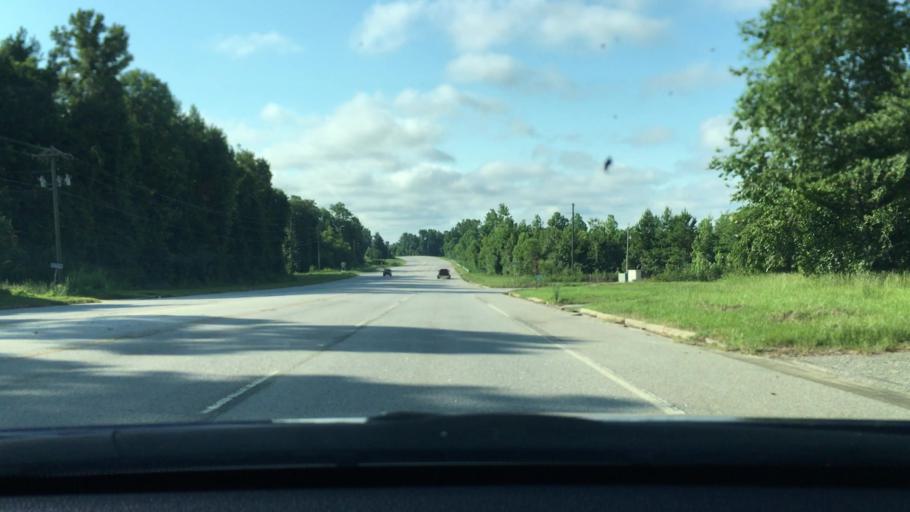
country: US
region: South Carolina
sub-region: Clarendon County
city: Manning
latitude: 33.7536
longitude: -80.2232
